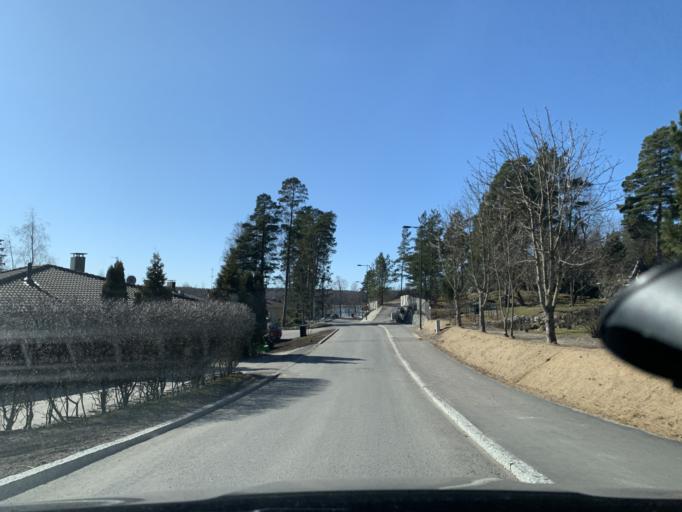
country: FI
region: Uusimaa
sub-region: Helsinki
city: Espoo
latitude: 60.1658
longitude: 24.6038
